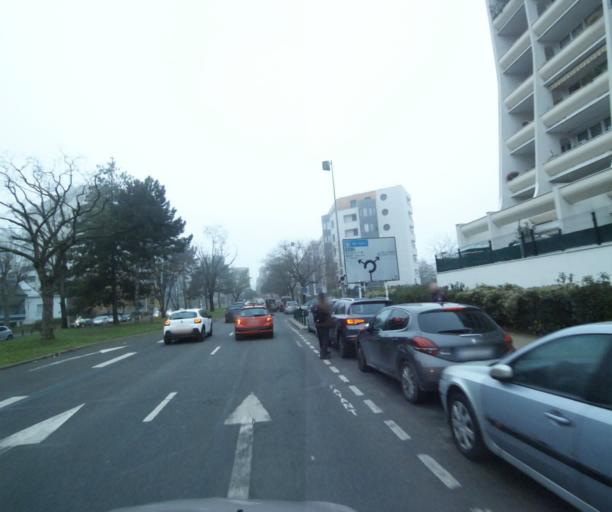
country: FR
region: Ile-de-France
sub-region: Departement du Val-de-Marne
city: Villiers-sur-Marne
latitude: 48.8421
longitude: 2.5494
